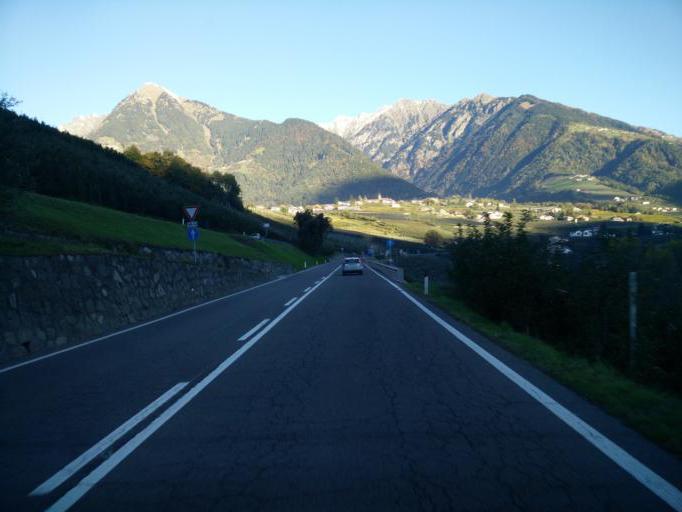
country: IT
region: Trentino-Alto Adige
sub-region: Bolzano
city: Merano
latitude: 46.6785
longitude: 11.1695
